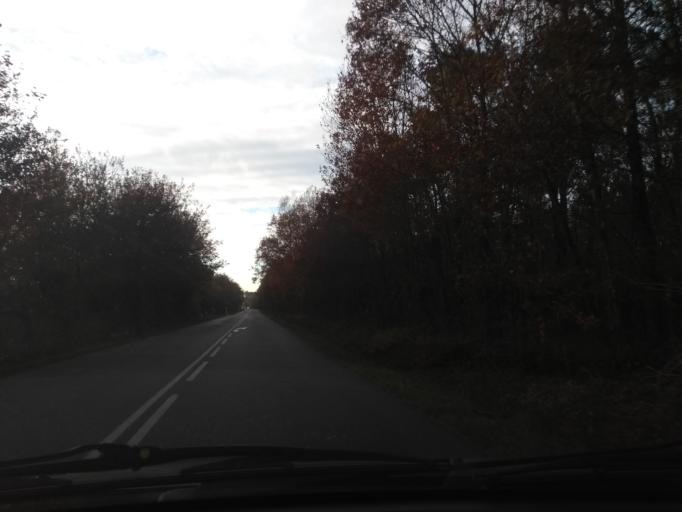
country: FR
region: Aquitaine
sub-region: Departement de la Gironde
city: Le Barp
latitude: 44.5932
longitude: -0.7221
